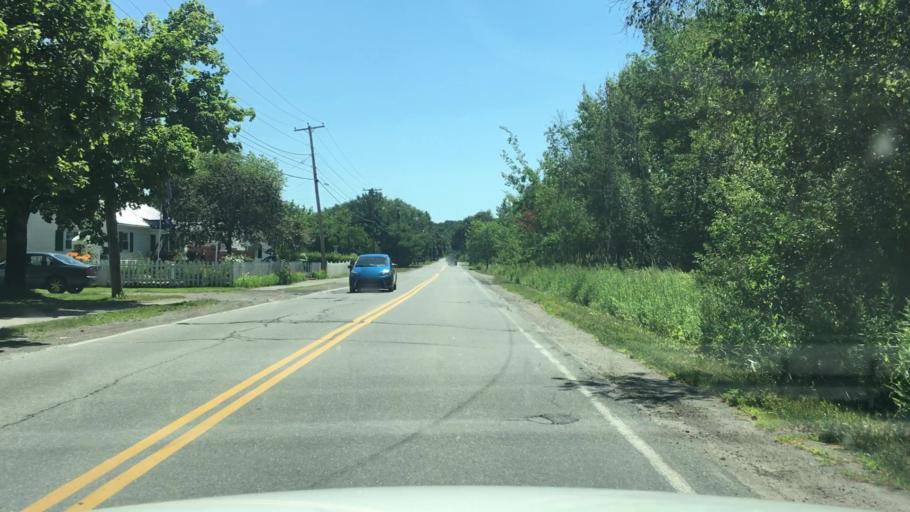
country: US
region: Maine
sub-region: Penobscot County
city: Bangor
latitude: 44.8191
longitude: -68.7900
